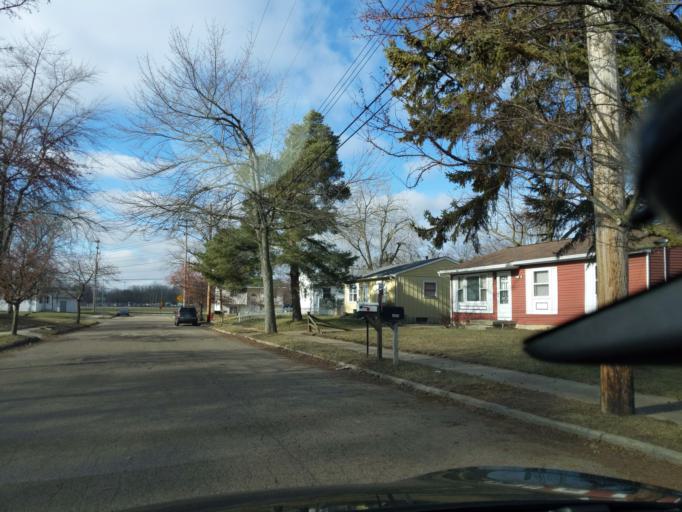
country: US
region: Michigan
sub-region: Ingham County
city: Lansing
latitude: 42.6758
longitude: -84.5856
